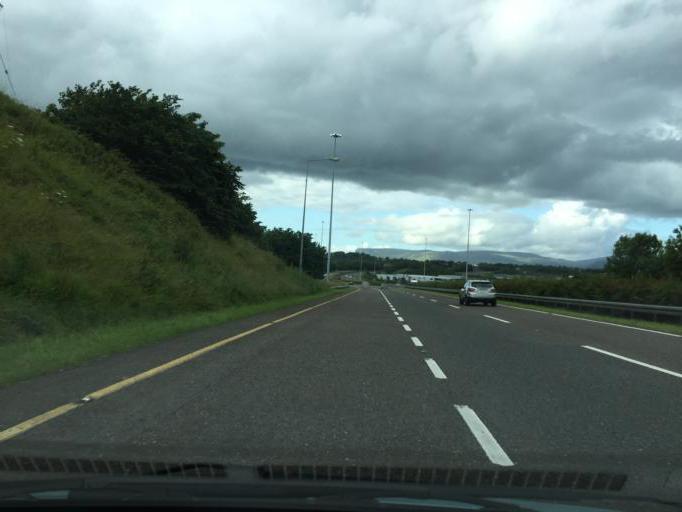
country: IE
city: Ballisodare
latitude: 54.2179
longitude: -8.5003
